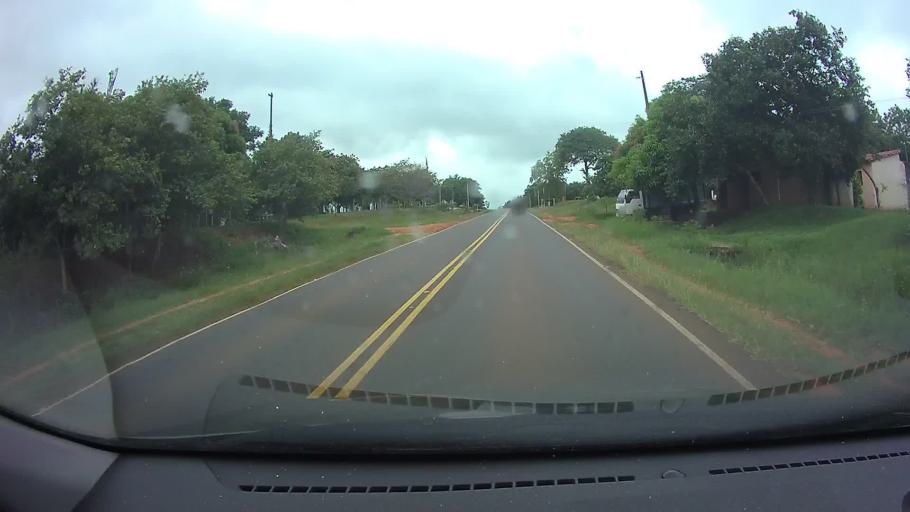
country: PY
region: Paraguari
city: Carapegua
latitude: -25.7374
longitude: -57.2927
